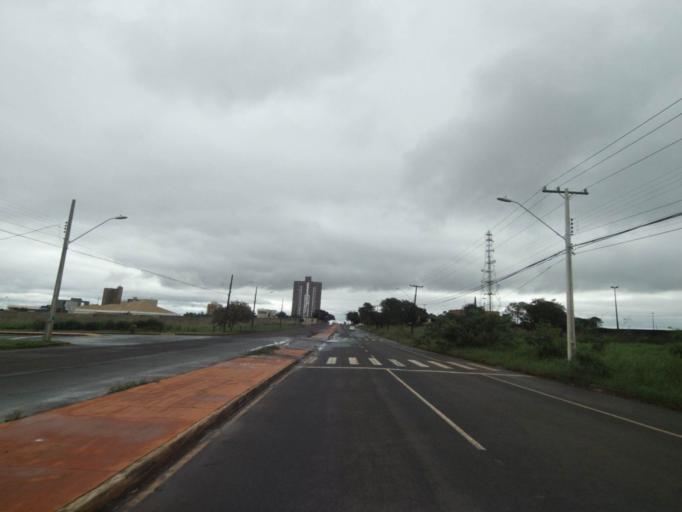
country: BR
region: Parana
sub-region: Foz Do Iguacu
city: Foz do Iguacu
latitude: -25.5181
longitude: -54.5667
